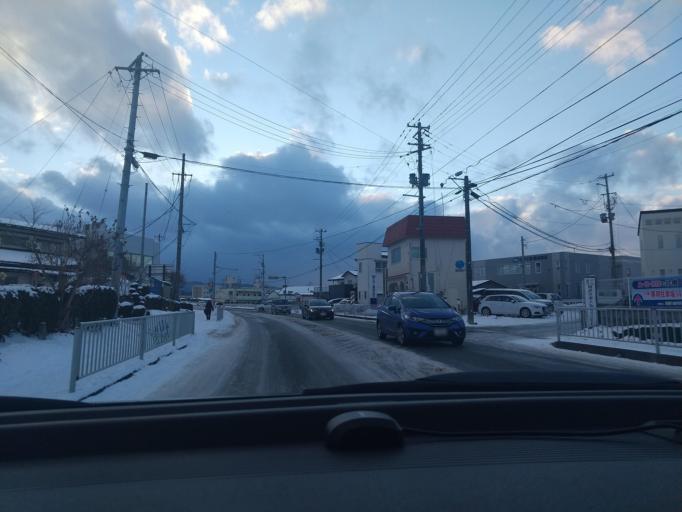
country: JP
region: Iwate
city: Morioka-shi
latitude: 39.7115
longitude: 141.1190
